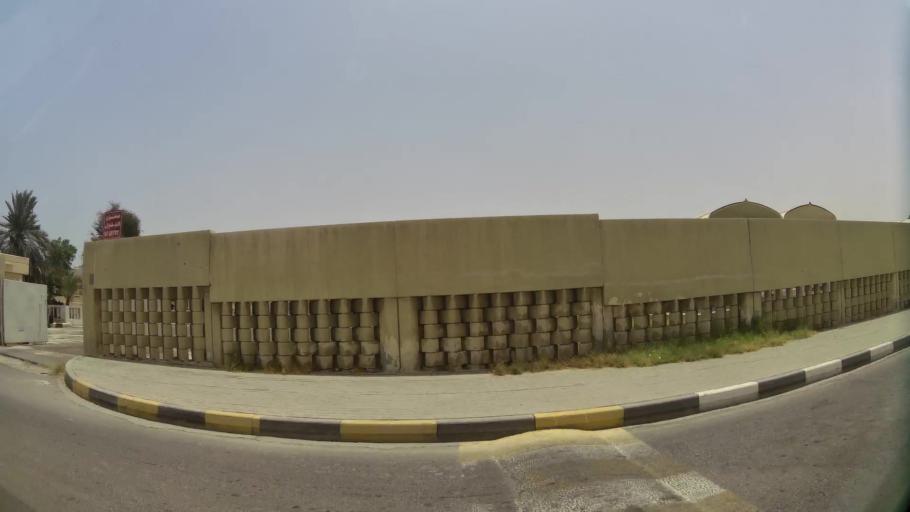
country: AE
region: Ash Shariqah
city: Sharjah
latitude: 25.3519
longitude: 55.3944
